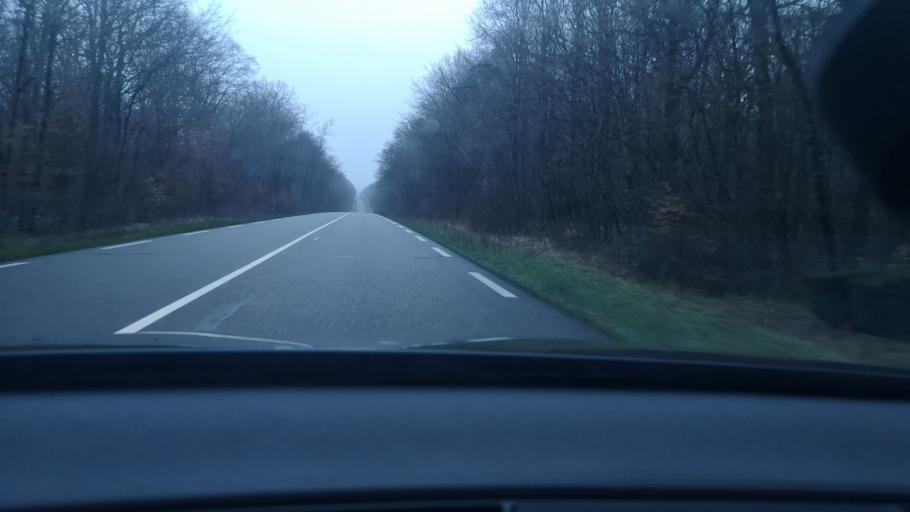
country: FR
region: Bourgogne
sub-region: Departement de la Cote-d'Or
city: Aiserey
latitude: 47.1047
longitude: 5.1025
